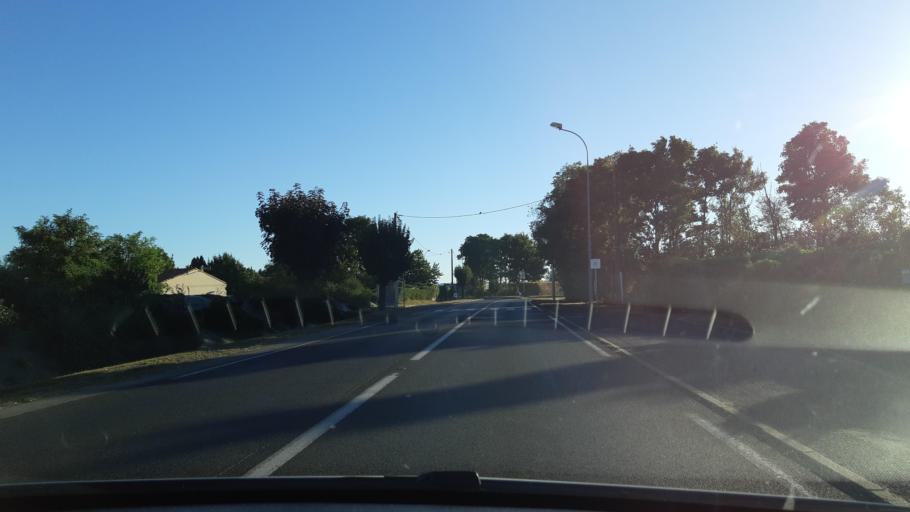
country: FR
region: Poitou-Charentes
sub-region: Departement des Deux-Sevres
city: La Creche
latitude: 46.3684
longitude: -0.2910
